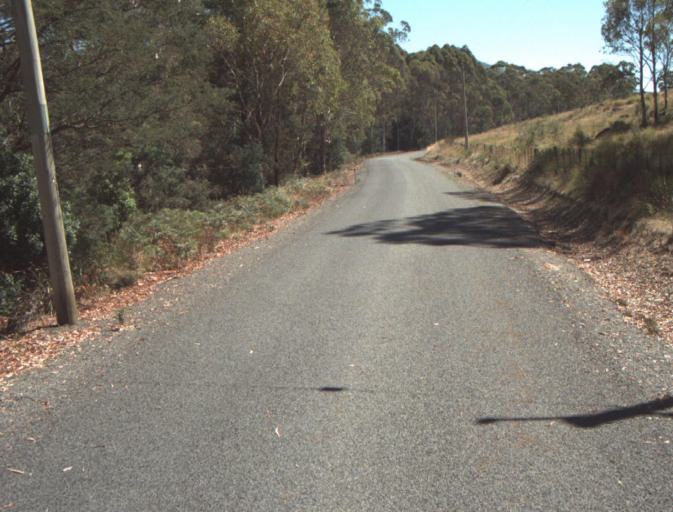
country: AU
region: Tasmania
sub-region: Launceston
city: Newstead
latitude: -41.3616
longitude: 147.3023
